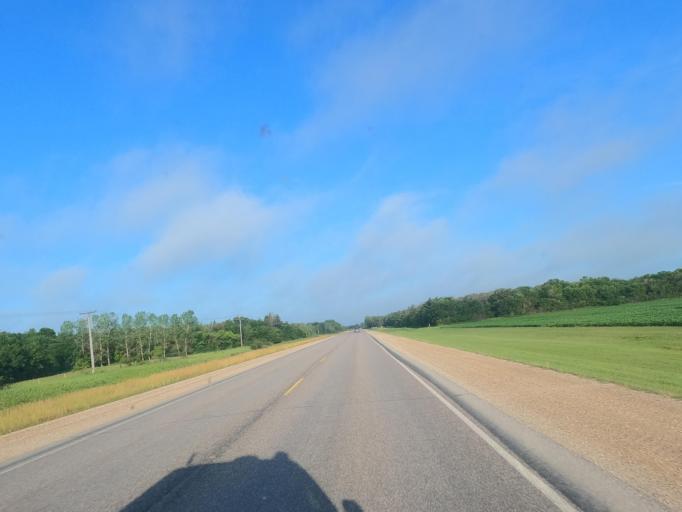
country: CA
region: Manitoba
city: Headingley
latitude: 49.7687
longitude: -97.5826
